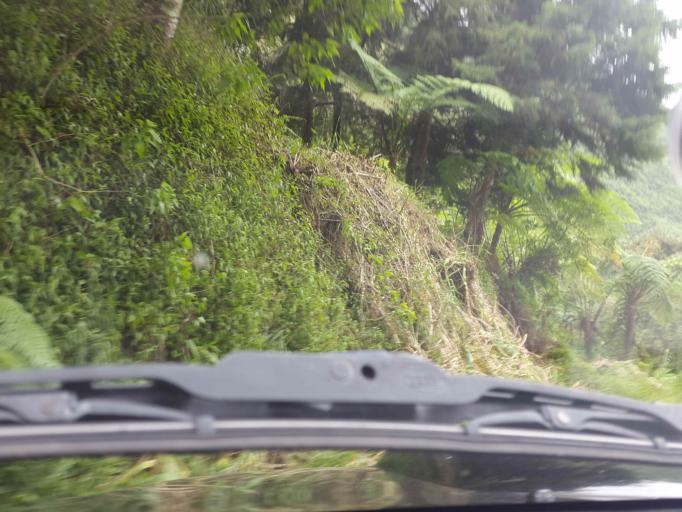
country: ID
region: Central Java
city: Wonosobo
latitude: -7.2434
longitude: 109.9058
